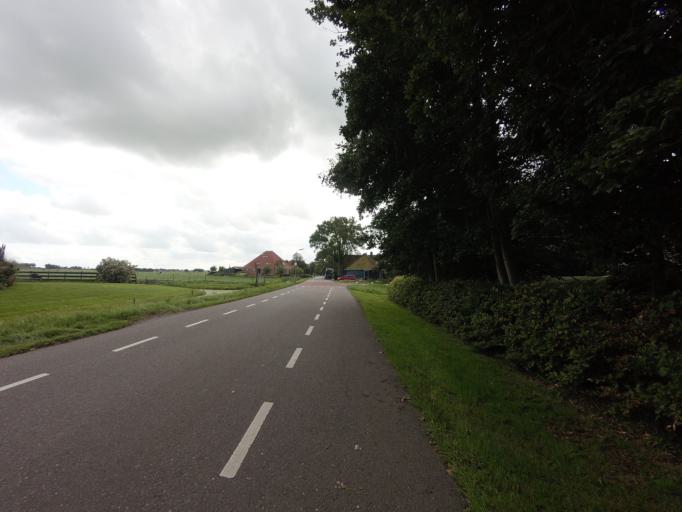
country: NL
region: North Holland
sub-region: Gemeente Edam-Volendam
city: Edam
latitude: 52.5385
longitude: 5.0140
